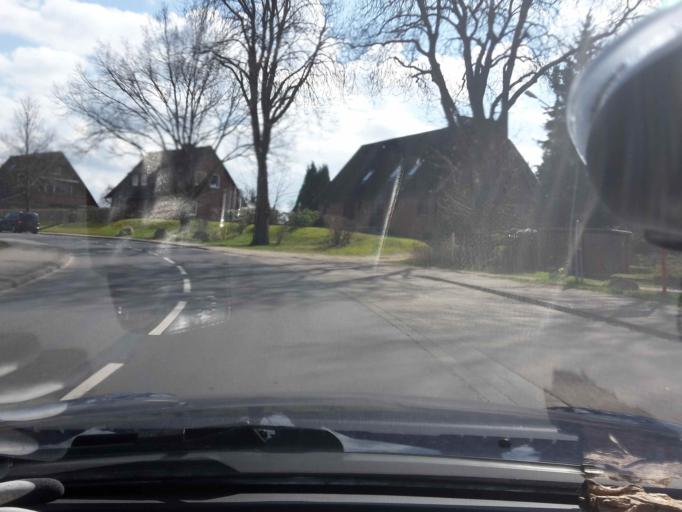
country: DE
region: Lower Saxony
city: Asendorf
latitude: 53.2899
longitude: 9.9796
